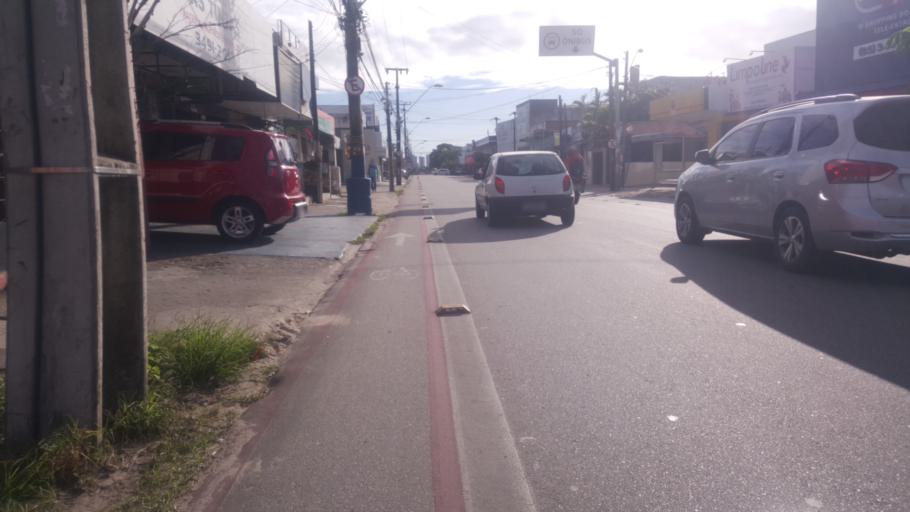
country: BR
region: Ceara
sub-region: Fortaleza
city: Fortaleza
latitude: -3.7617
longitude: -38.5460
